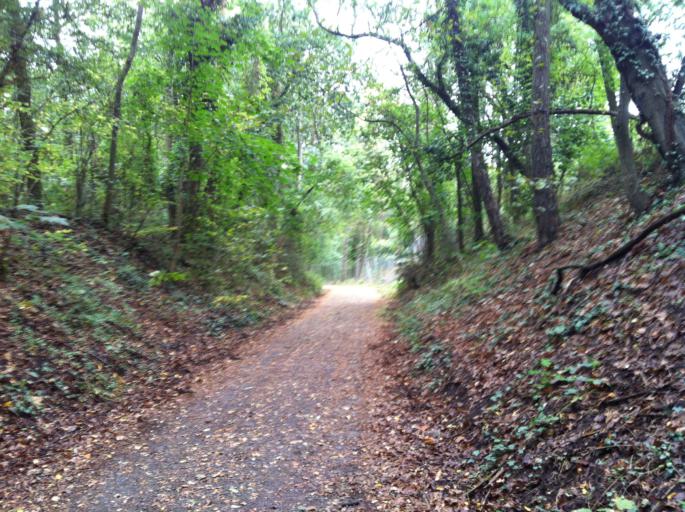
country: DE
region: Rheinland-Pfalz
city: Budenheim
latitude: 50.0127
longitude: 8.1762
